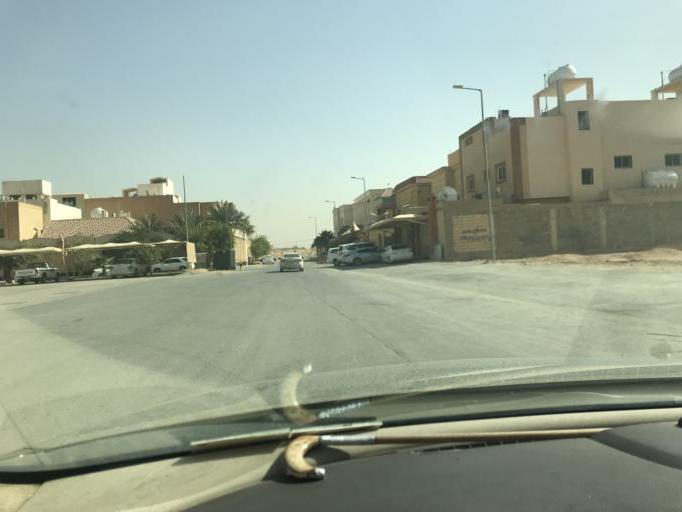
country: SA
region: Ar Riyad
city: Riyadh
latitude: 24.8272
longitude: 46.7307
